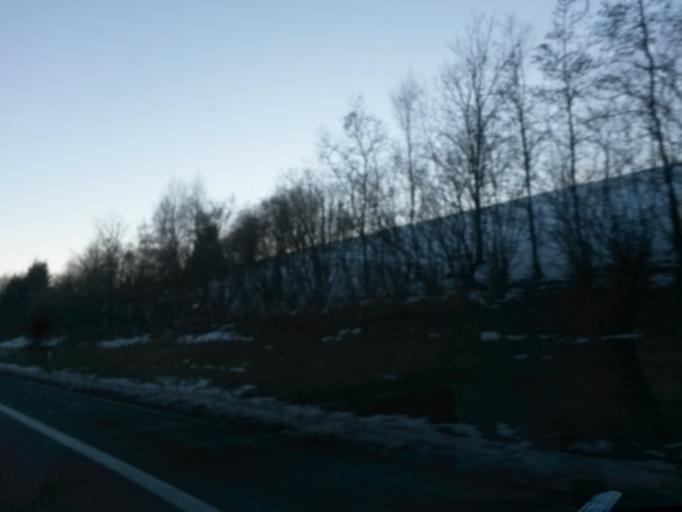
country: BE
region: Wallonia
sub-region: Province de Liege
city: Saint-Vith
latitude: 50.3081
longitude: 6.0800
